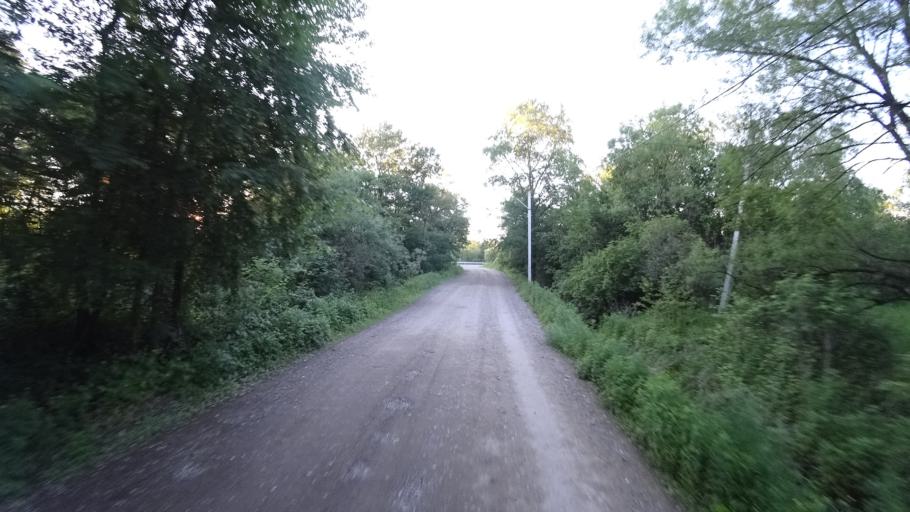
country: RU
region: Khabarovsk Krai
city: Khor
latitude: 47.8524
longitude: 134.9829
